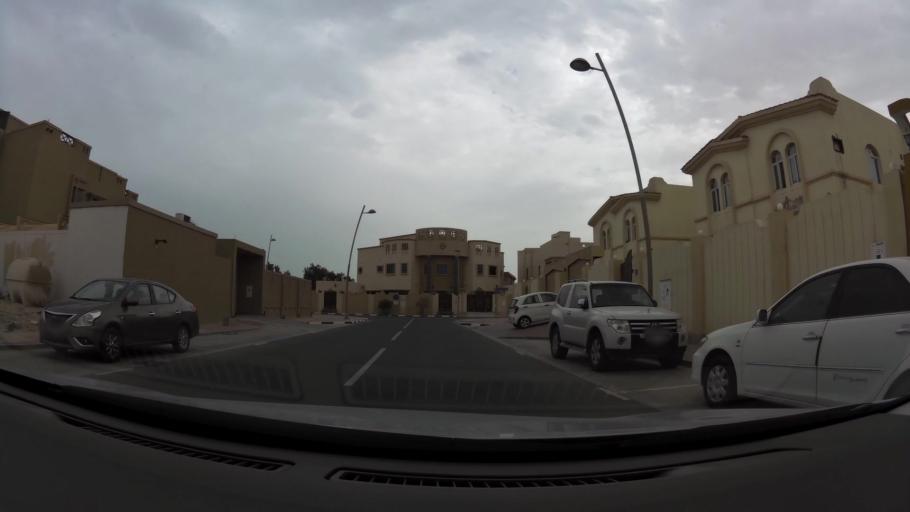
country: QA
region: Baladiyat ad Dawhah
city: Doha
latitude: 25.3423
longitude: 51.4840
